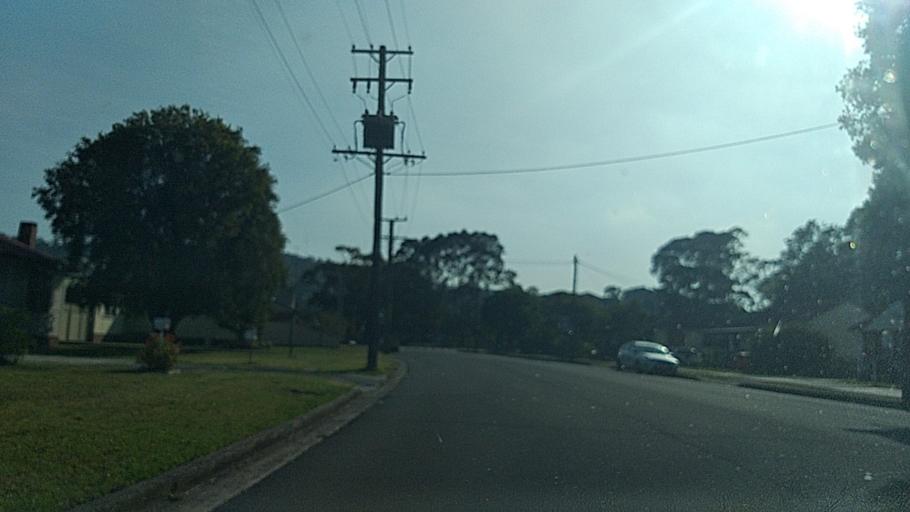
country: AU
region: New South Wales
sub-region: Wollongong
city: Berkeley
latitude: -34.4790
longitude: 150.8529
